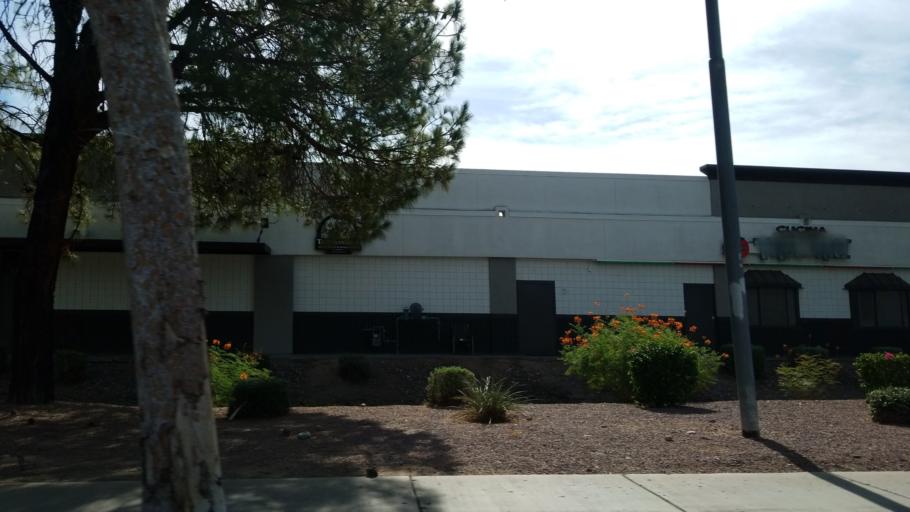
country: US
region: Arizona
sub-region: Maricopa County
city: Peoria
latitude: 33.6403
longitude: -112.1864
